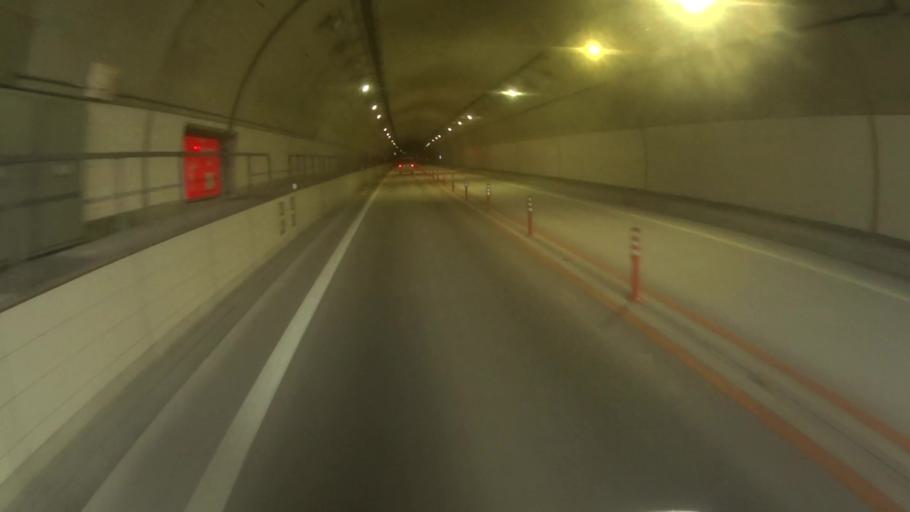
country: JP
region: Kyoto
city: Miyazu
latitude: 35.5413
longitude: 135.1566
